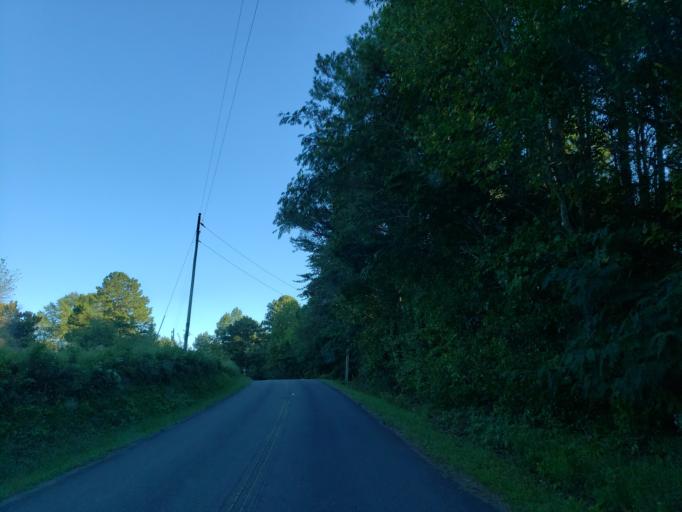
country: US
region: Georgia
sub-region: Bartow County
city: Rydal
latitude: 34.3971
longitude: -84.6716
